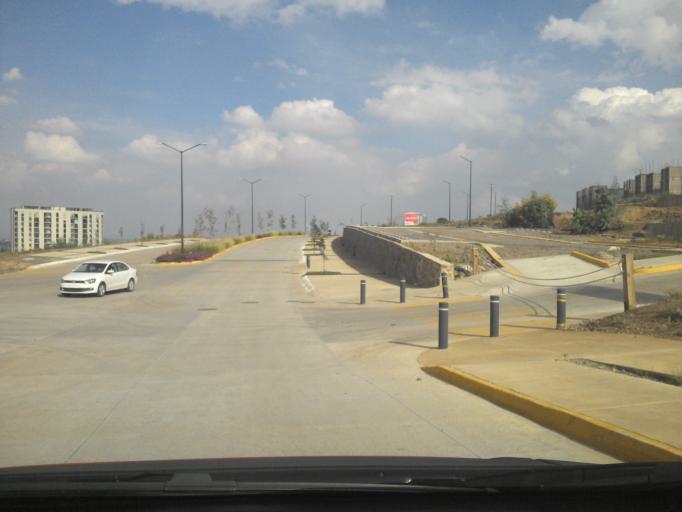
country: MX
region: Jalisco
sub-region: Tlajomulco de Zuniga
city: Altus Bosques
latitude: 20.6081
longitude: -103.3635
